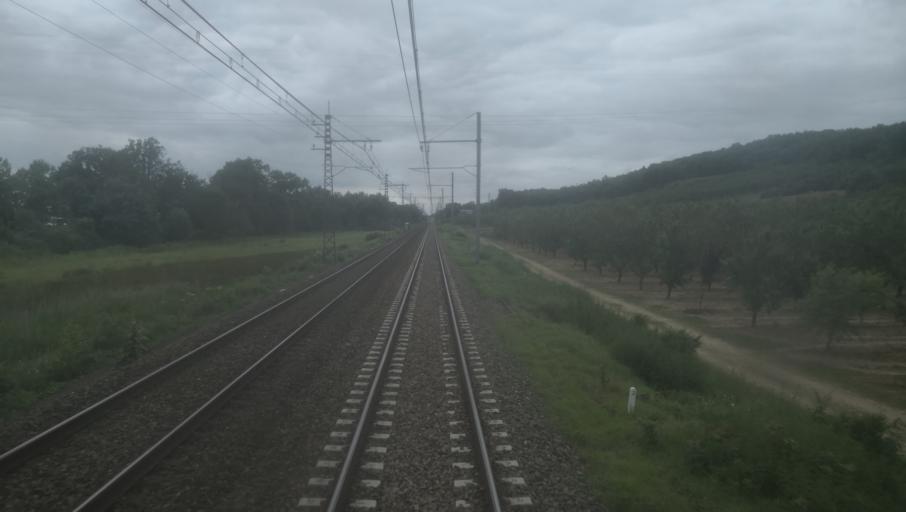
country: FR
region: Midi-Pyrenees
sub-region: Departement du Tarn-et-Garonne
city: Grisolles
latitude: 43.8539
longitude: 1.2848
